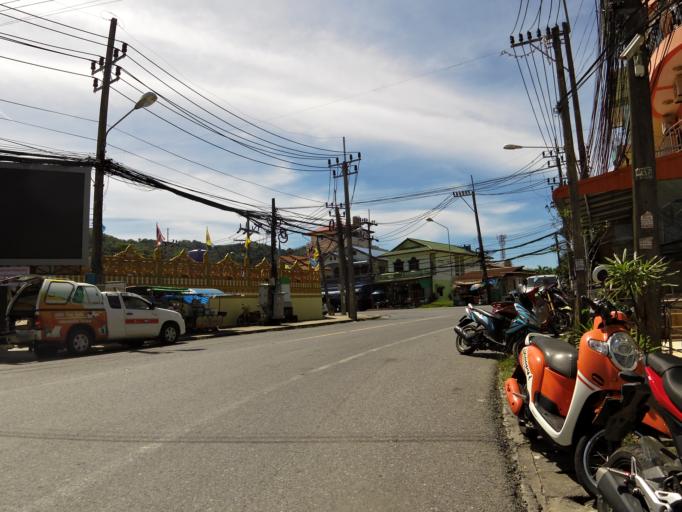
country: TH
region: Phuket
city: Ban Karon
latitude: 7.8480
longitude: 98.2973
